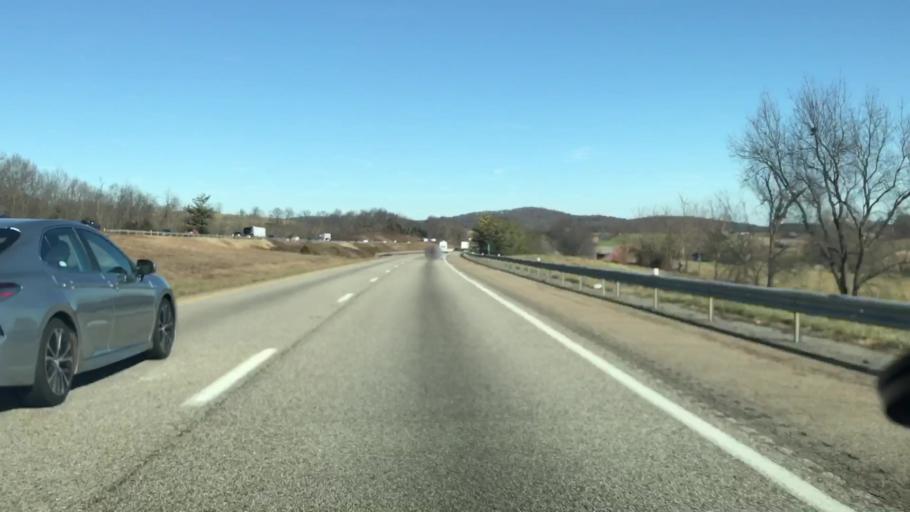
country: US
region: Virginia
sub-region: Augusta County
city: Stuarts Draft
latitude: 37.9972
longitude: -79.1756
